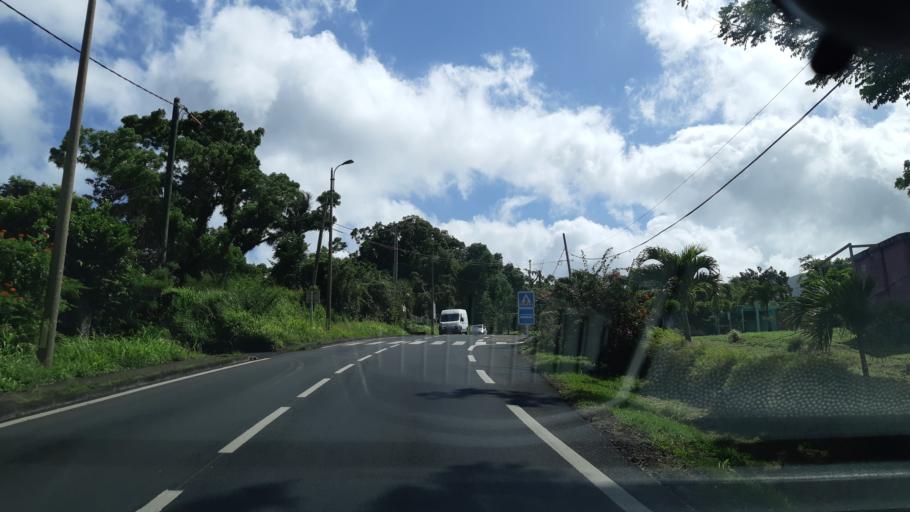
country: GP
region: Guadeloupe
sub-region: Guadeloupe
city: Saint-Claude
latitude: 16.0160
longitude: -61.7085
